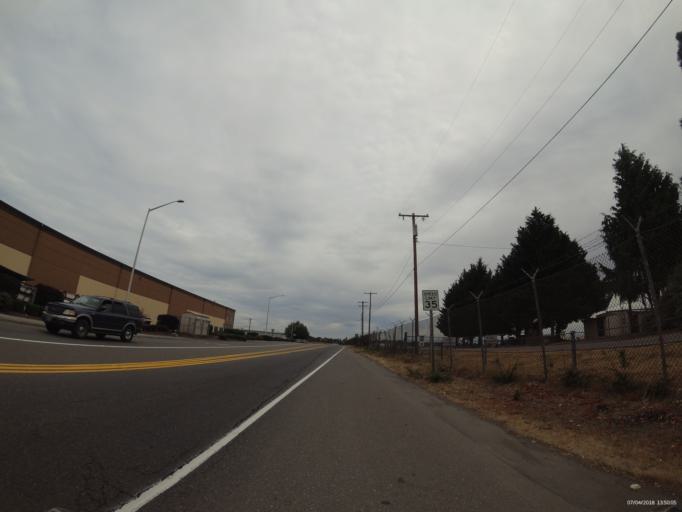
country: US
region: Washington
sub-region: Pierce County
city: McChord Air Force Base
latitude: 47.1557
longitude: -122.4826
